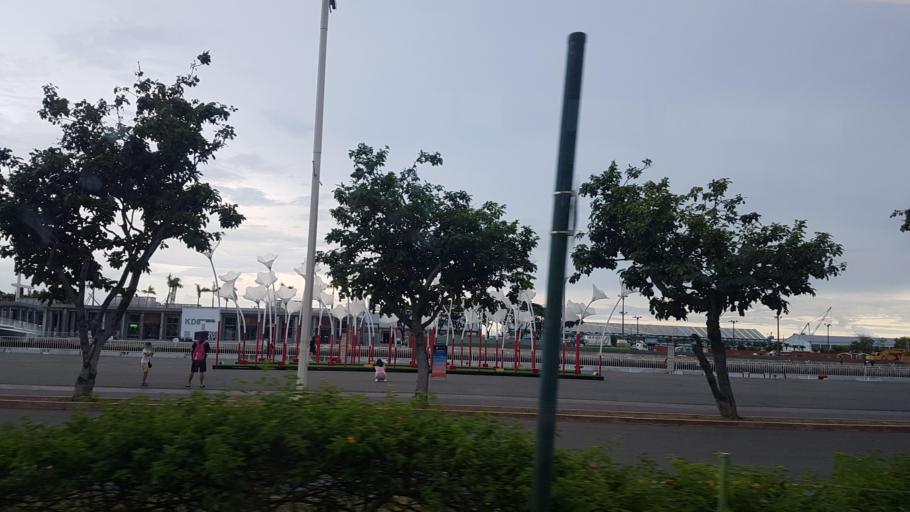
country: TW
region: Kaohsiung
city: Kaohsiung
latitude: 22.6186
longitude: 120.2837
